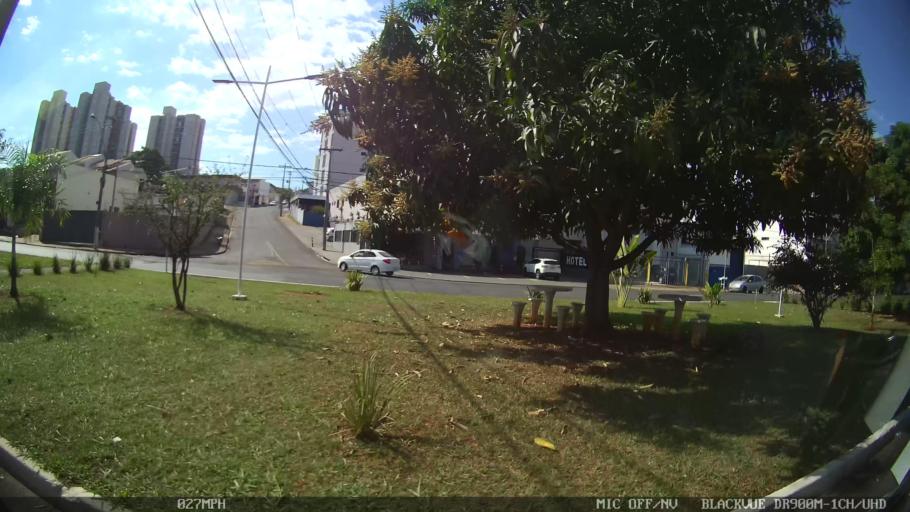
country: BR
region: Sao Paulo
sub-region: Americana
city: Americana
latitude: -22.7407
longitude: -47.3080
